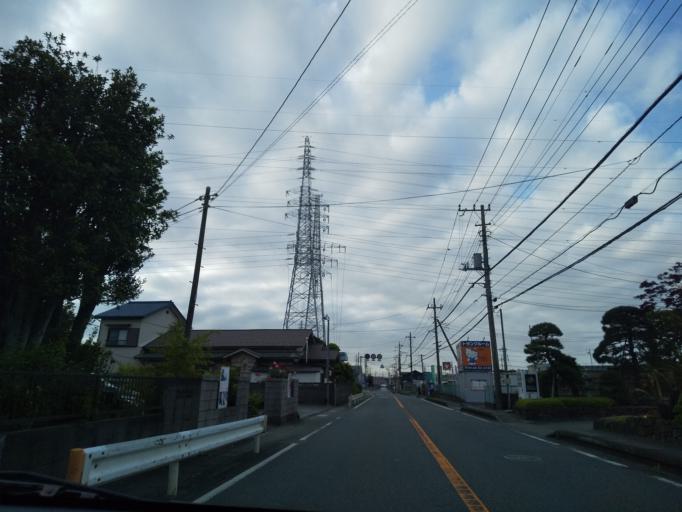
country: JP
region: Kanagawa
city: Zama
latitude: 35.5365
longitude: 139.3695
